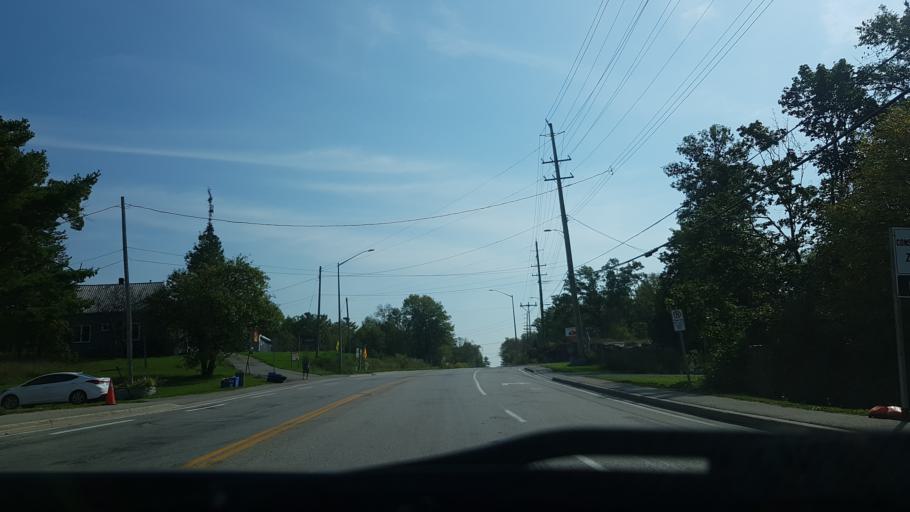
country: CA
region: Ontario
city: Orillia
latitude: 44.7487
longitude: -79.3319
